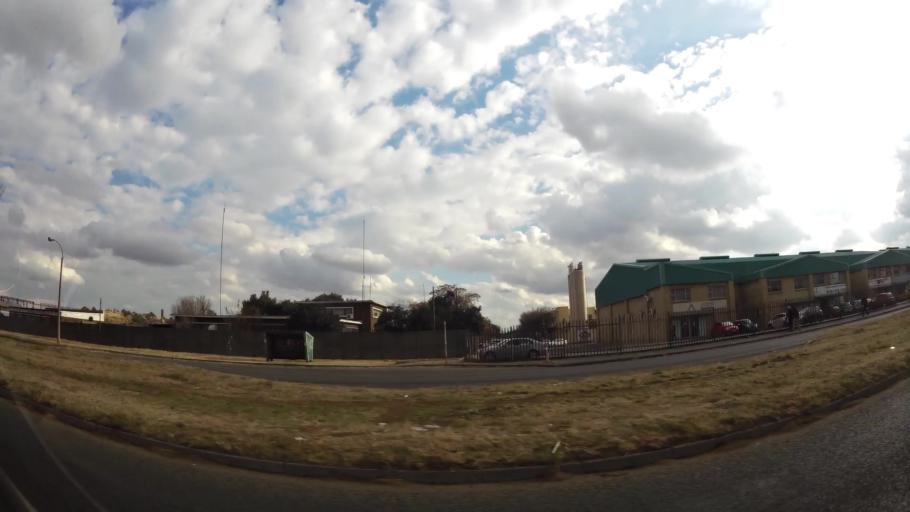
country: ZA
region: Orange Free State
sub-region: Fezile Dabi District Municipality
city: Sasolburg
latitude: -26.8234
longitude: 27.8360
